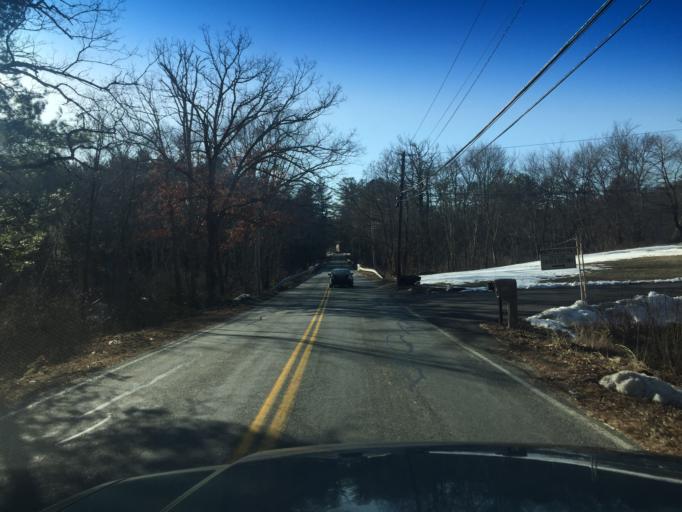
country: US
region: Massachusetts
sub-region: Worcester County
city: Mendon
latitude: 42.0931
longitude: -71.5167
